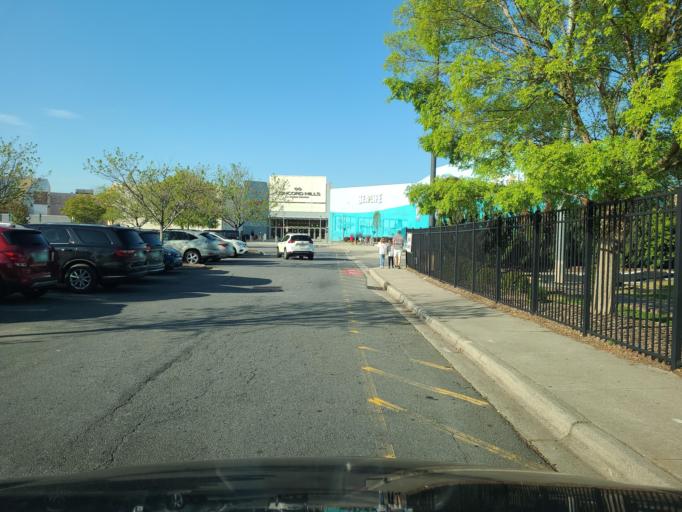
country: US
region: North Carolina
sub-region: Cabarrus County
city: Harrisburg
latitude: 35.3688
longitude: -80.7256
